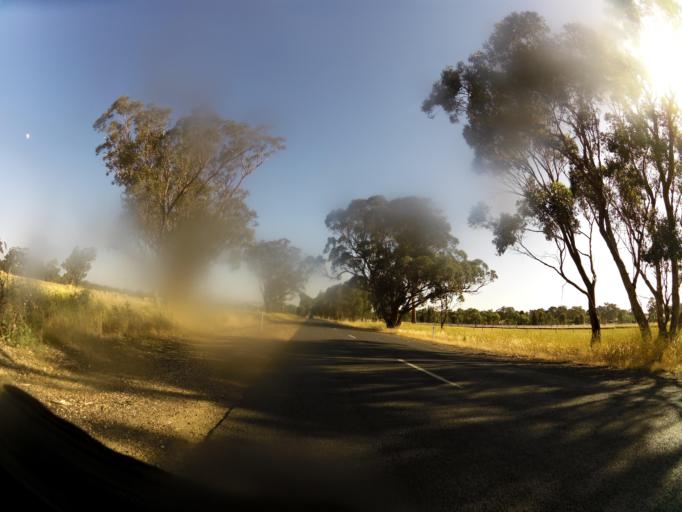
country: AU
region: Victoria
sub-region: Murrindindi
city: Kinglake West
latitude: -36.9825
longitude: 145.1111
